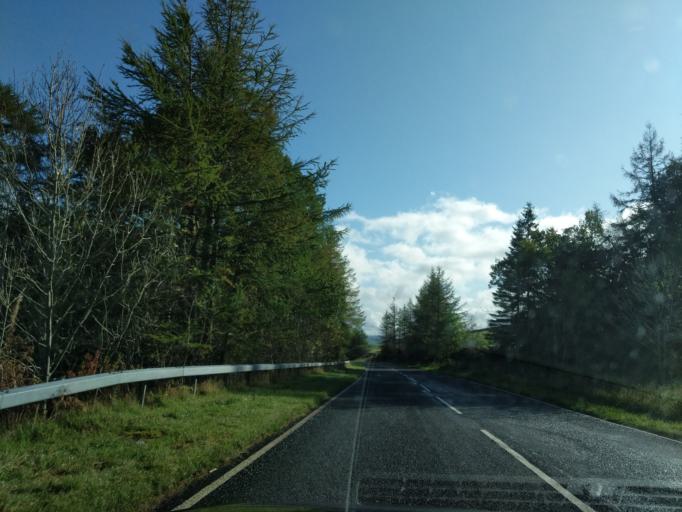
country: GB
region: Scotland
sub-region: Dumfries and Galloway
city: Moffat
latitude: 55.3562
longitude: -3.4709
